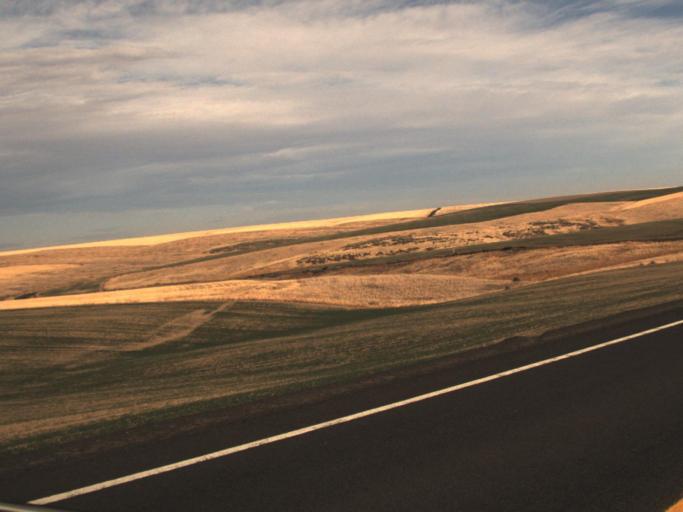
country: US
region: Washington
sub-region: Adams County
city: Ritzville
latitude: 47.1655
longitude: -118.6861
